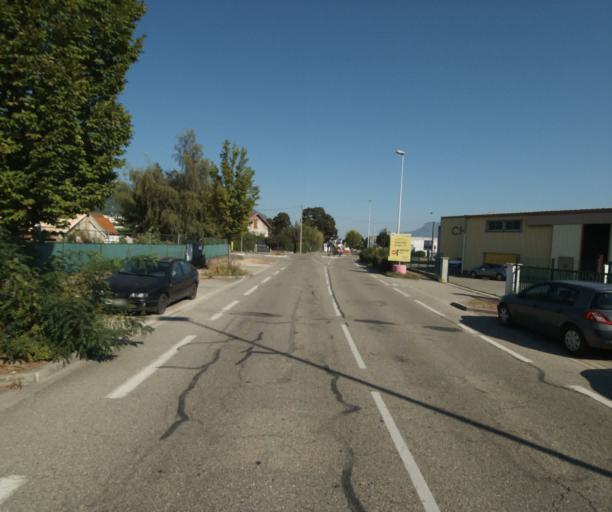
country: FR
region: Rhone-Alpes
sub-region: Departement de l'Isere
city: Le Pont-de-Claix
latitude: 45.1421
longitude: 5.7091
